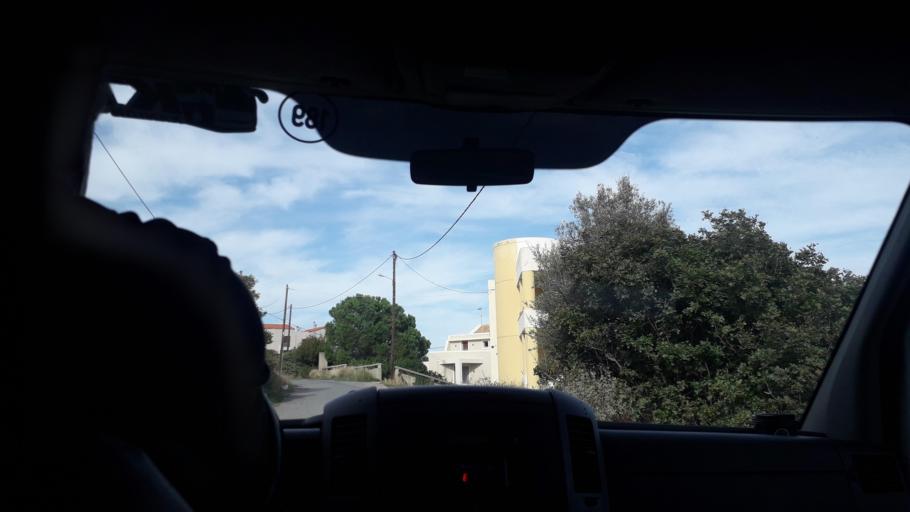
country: GR
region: Crete
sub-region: Nomos Rethymnis
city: Atsipopoulon
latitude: 35.3629
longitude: 24.4377
